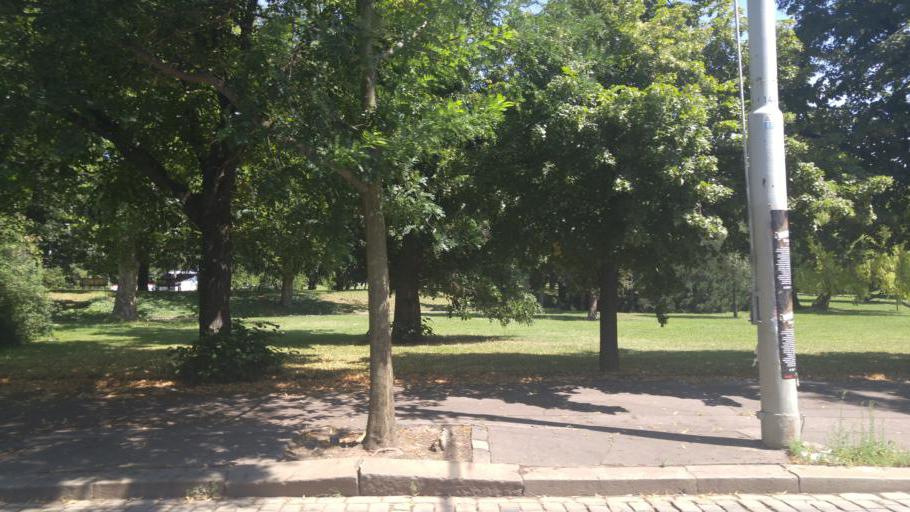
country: CZ
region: Praha
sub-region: Praha 1
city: Mala Strana
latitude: 50.0960
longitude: 14.4085
